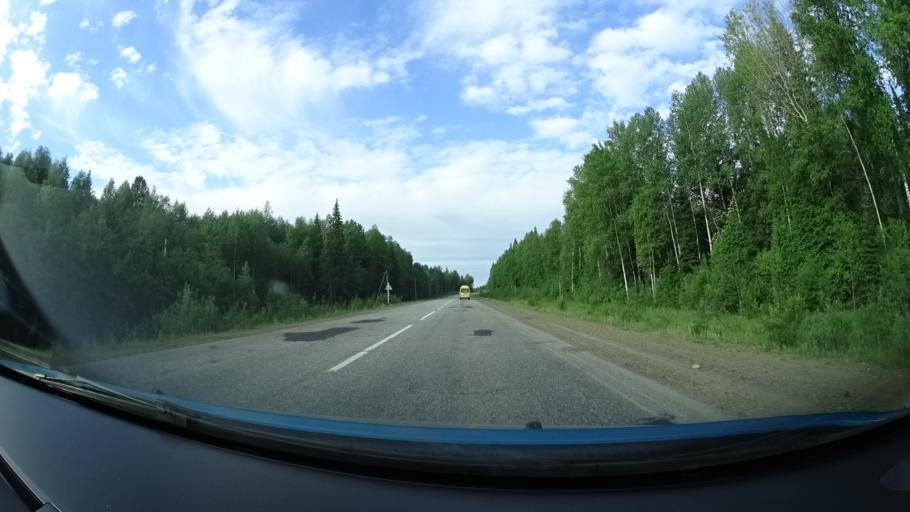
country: RU
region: Perm
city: Osa
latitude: 57.4366
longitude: 55.6270
